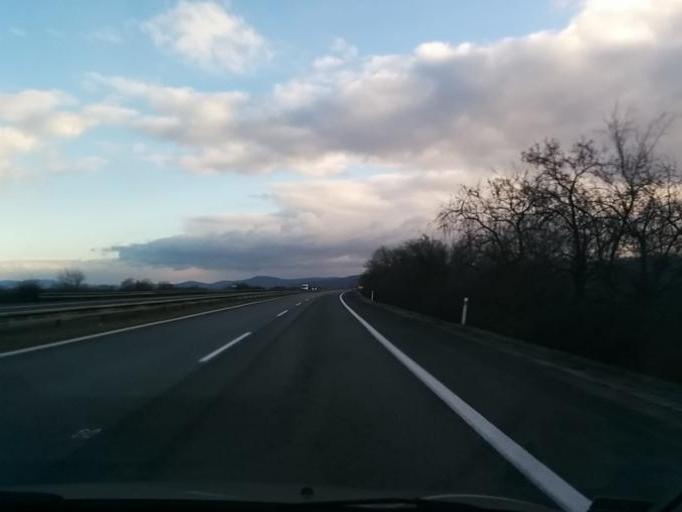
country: SK
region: Trnavsky
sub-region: Okres Trnava
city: Piestany
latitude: 48.6411
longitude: 17.8168
